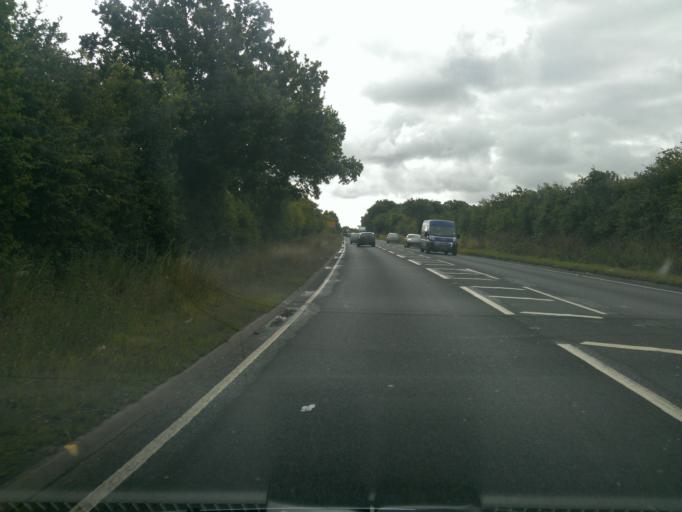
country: GB
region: England
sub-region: Essex
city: Great Bentley
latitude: 51.8708
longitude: 1.0573
